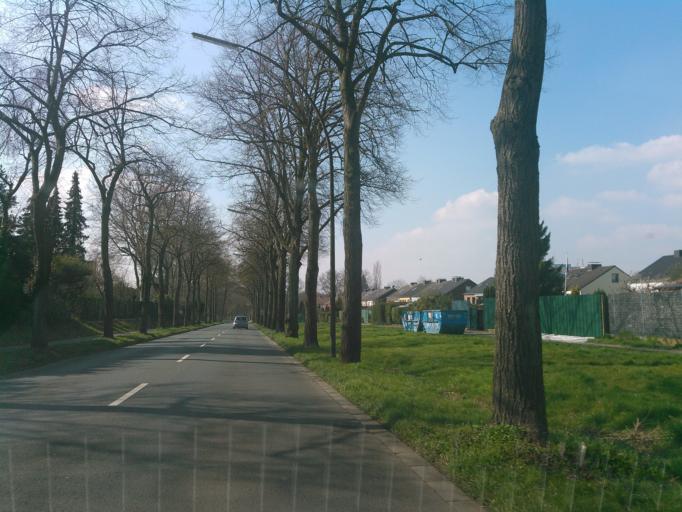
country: DE
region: North Rhine-Westphalia
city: Marl
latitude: 51.6540
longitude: 7.0797
